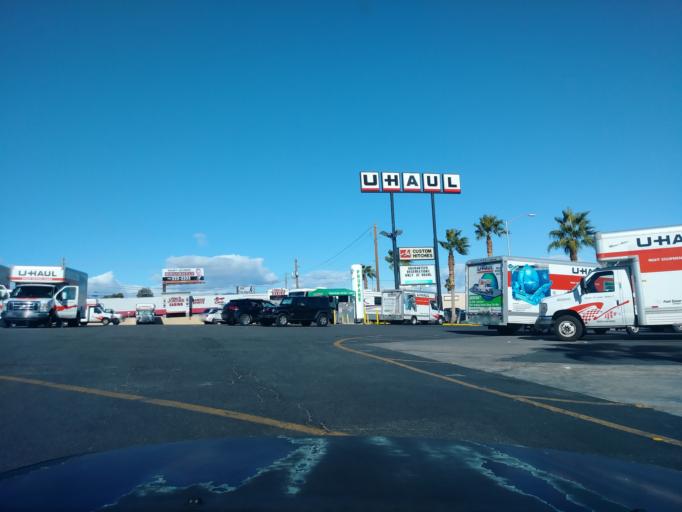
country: US
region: Nevada
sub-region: Clark County
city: Spring Valley
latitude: 36.1503
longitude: -115.2084
